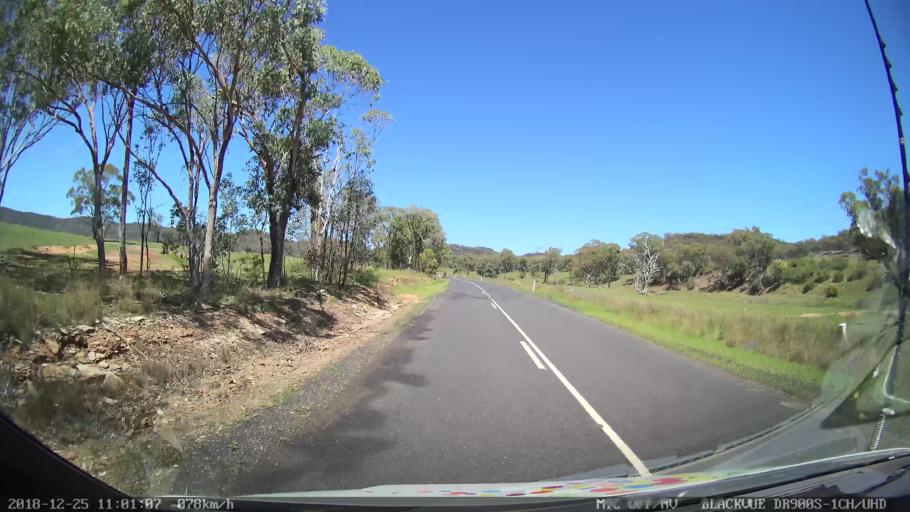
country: AU
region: New South Wales
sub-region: Upper Hunter Shire
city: Merriwa
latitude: -32.4036
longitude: 150.2058
